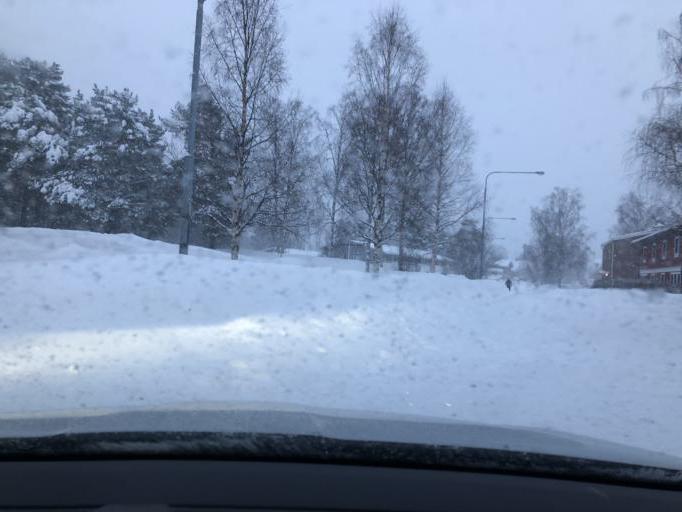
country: SE
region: Vaesterbotten
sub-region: Skelleftea Kommun
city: Burea
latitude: 64.6178
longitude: 21.2028
